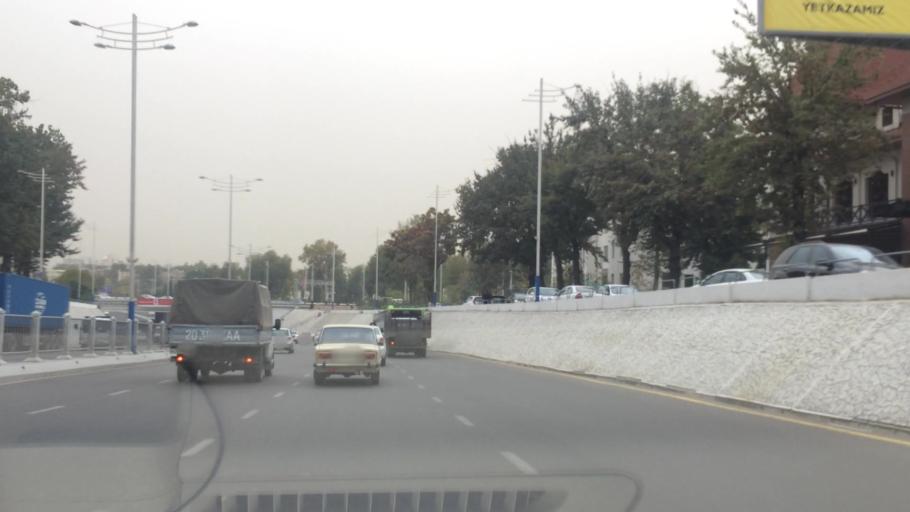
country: UZ
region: Toshkent Shahri
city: Tashkent
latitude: 41.3065
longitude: 69.3047
